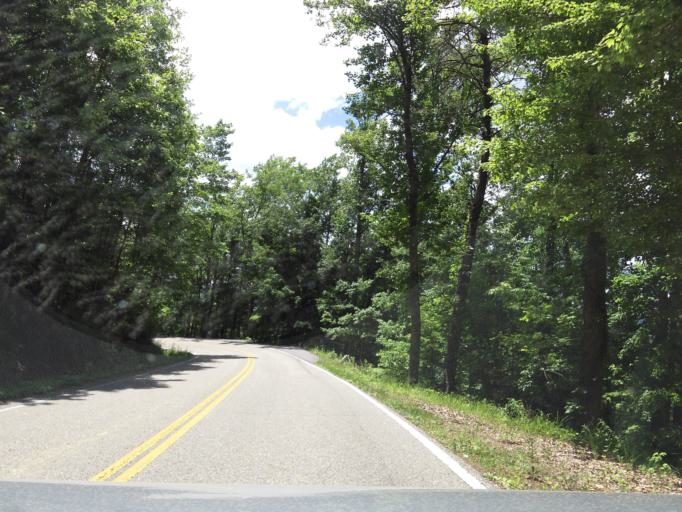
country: US
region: North Carolina
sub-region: Graham County
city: Robbinsville
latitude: 35.5006
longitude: -83.9496
